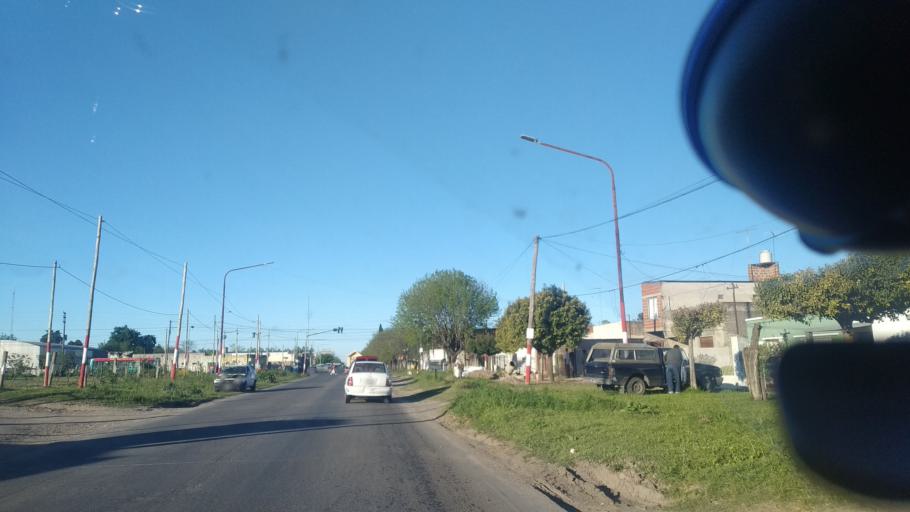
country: AR
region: Buenos Aires
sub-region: Partido de La Plata
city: La Plata
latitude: -34.9604
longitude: -57.9601
